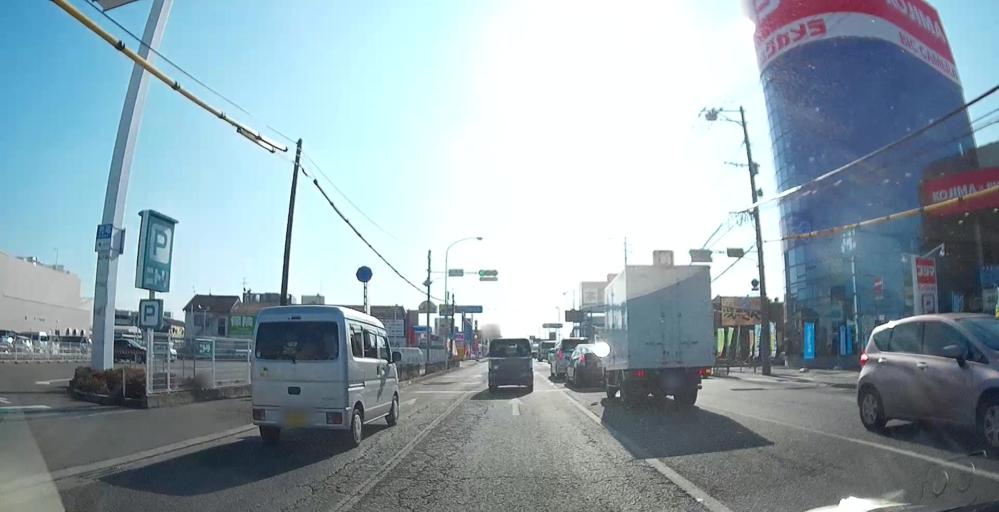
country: JP
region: Kumamoto
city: Kumamoto
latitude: 32.7605
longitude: 130.6891
